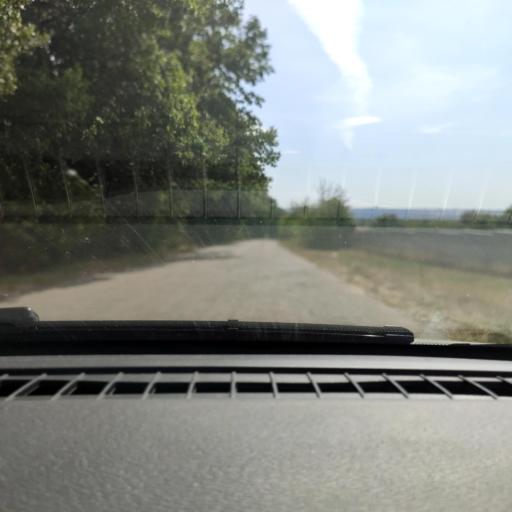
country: RU
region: Voronezj
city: Pridonskoy
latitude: 51.7381
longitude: 39.0573
